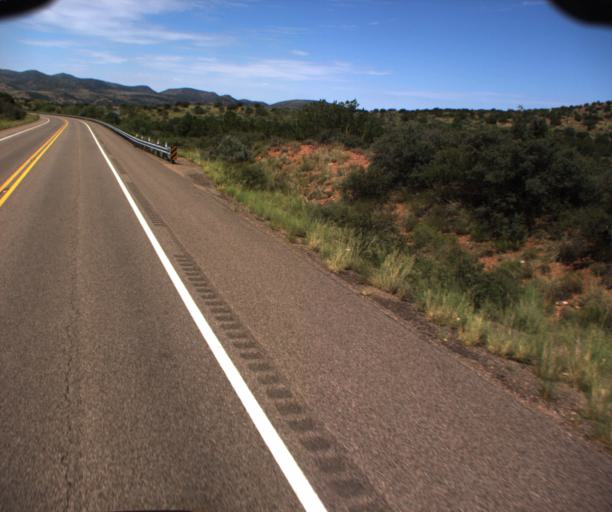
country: US
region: Arizona
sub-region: Gila County
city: Globe
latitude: 33.6114
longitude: -110.6214
